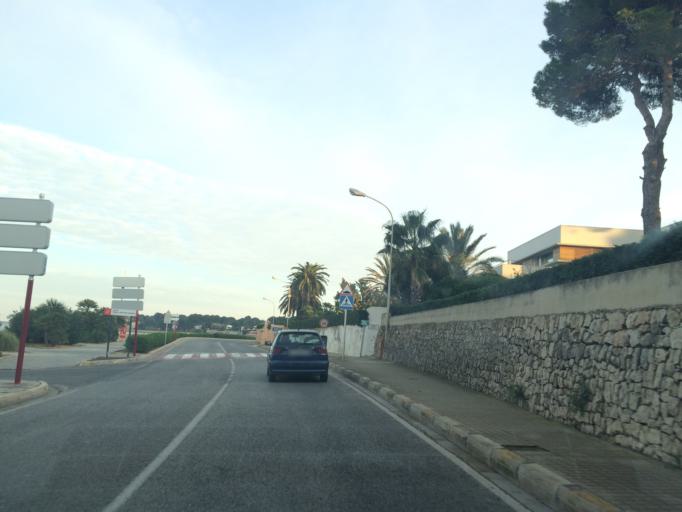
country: ES
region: Valencia
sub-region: Provincia de Alicante
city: Denia
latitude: 38.8343
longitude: 0.1221
